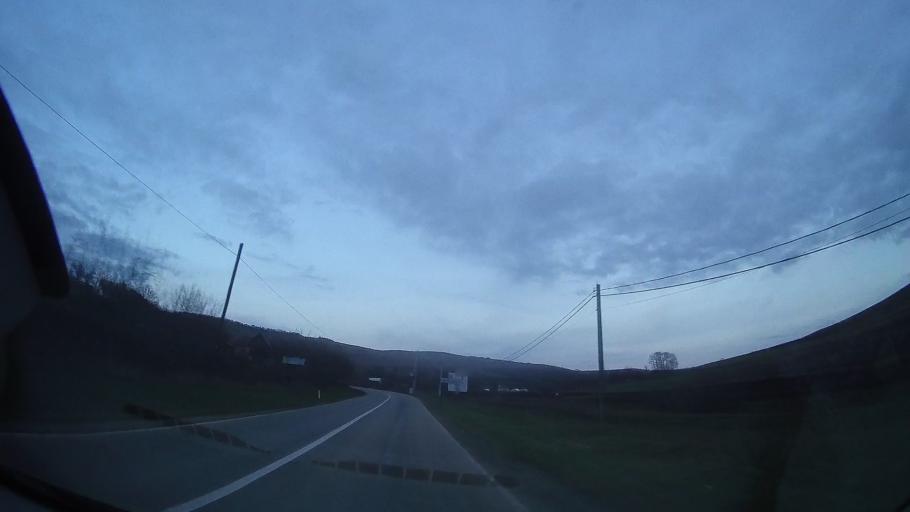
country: RO
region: Cluj
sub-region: Comuna Caianu
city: Vaida-Camaras
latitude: 46.8046
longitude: 23.9612
